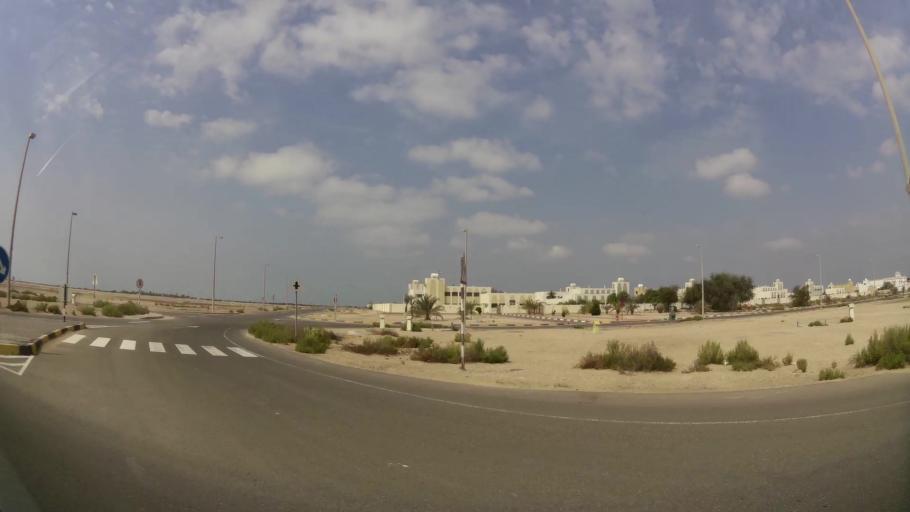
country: AE
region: Abu Dhabi
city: Abu Dhabi
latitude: 24.5841
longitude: 54.6505
